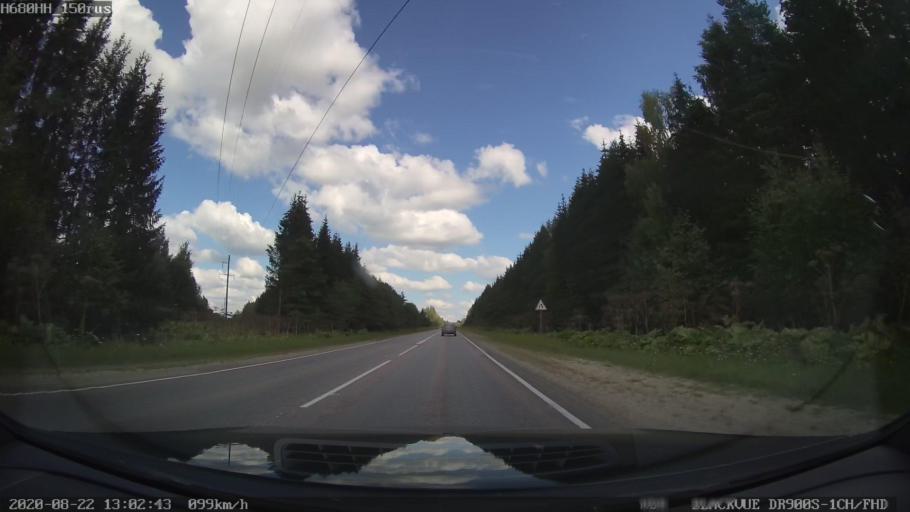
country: RU
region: Tverskaya
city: Bezhetsk
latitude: 57.6525
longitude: 36.4010
